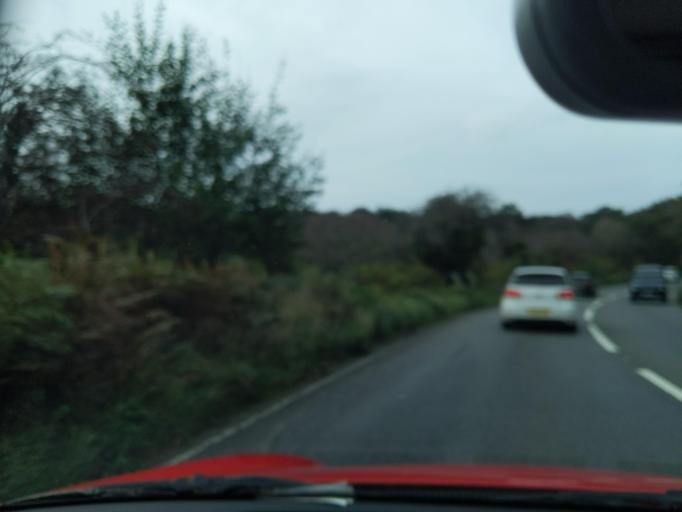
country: GB
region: England
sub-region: Devon
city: Yelverton
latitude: 50.4953
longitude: -4.0951
